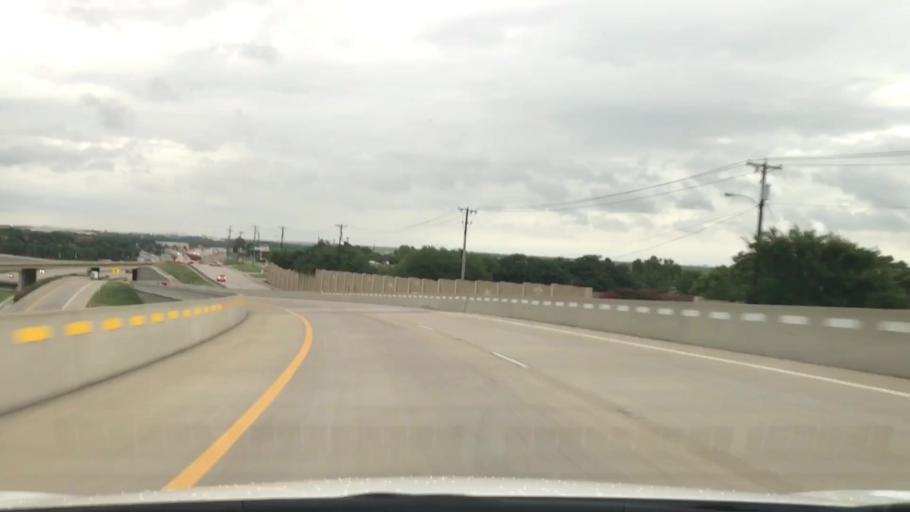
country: US
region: Texas
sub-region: Dallas County
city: Grand Prairie
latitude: 32.7612
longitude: -97.0286
